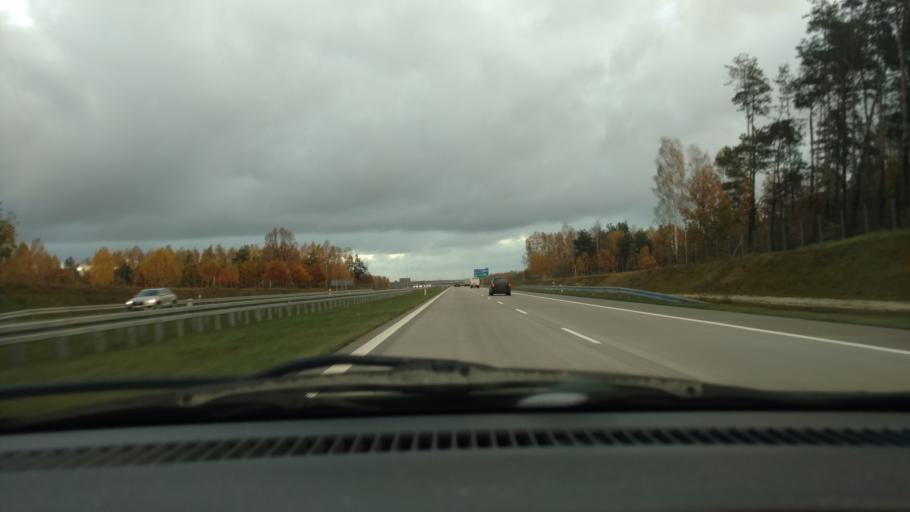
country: PL
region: Lodz Voivodeship
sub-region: Powiat lodzki wschodni
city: Brojce
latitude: 51.6659
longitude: 19.5851
